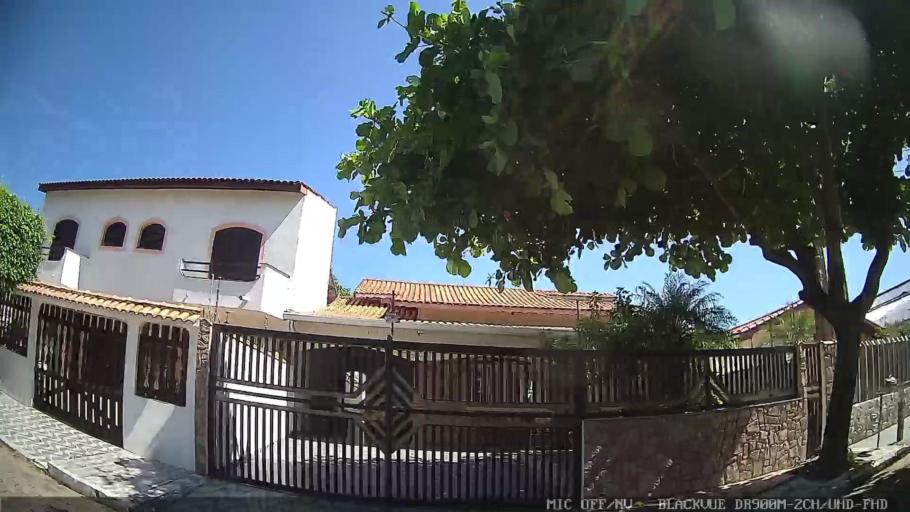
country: BR
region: Sao Paulo
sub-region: Peruibe
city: Peruibe
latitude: -24.3006
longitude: -46.9713
